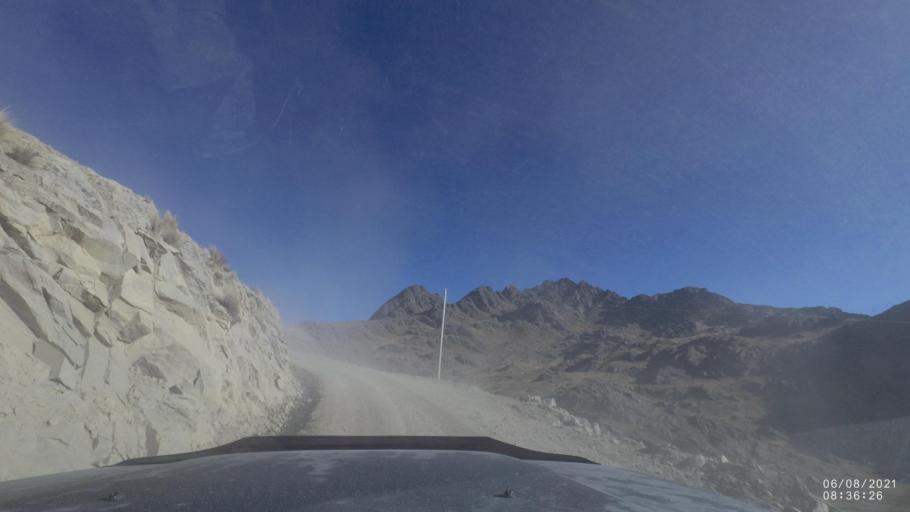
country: BO
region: Cochabamba
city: Sipe Sipe
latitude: -17.1774
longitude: -66.3846
